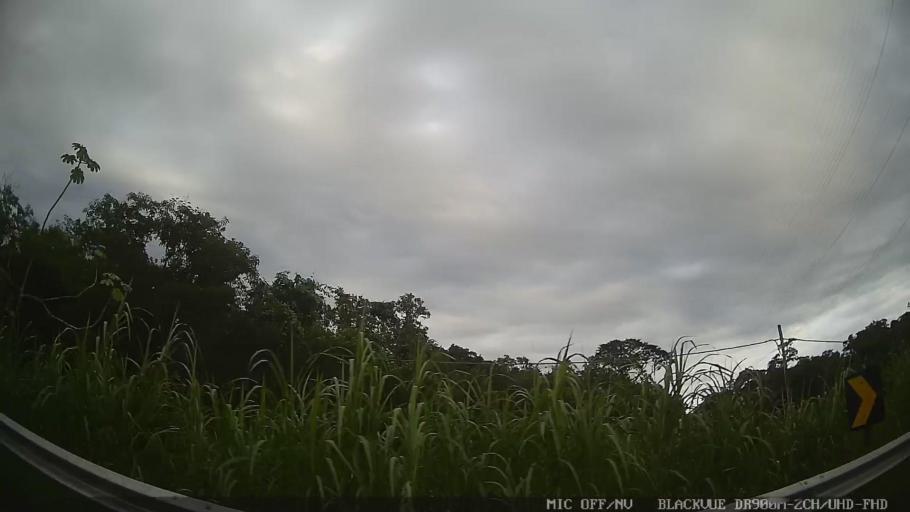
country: BR
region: Sao Paulo
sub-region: Bertioga
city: Bertioga
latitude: -23.7663
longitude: -46.0371
